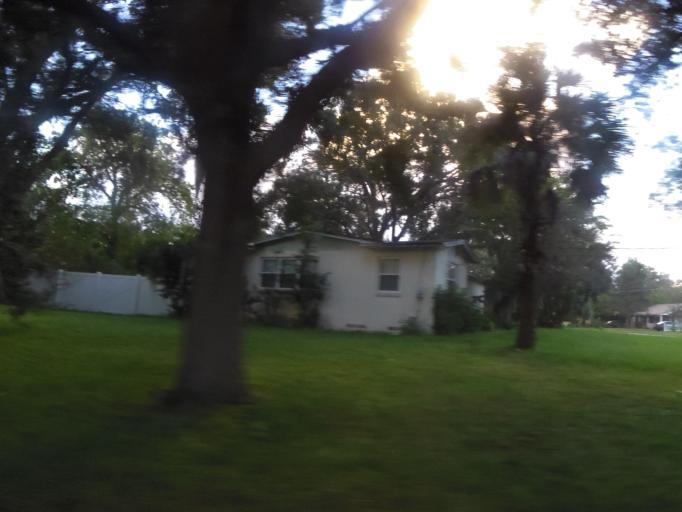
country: US
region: Florida
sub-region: Duval County
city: Jacksonville
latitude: 30.2381
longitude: -81.6102
